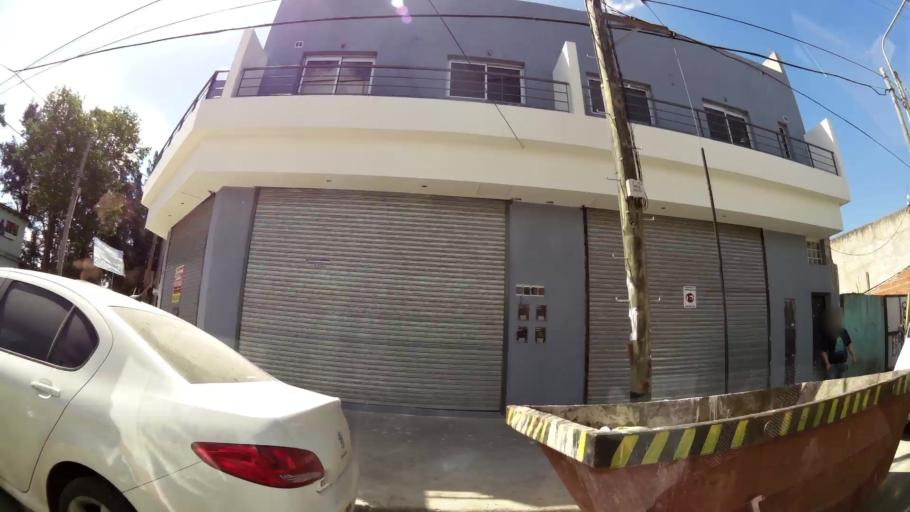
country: AR
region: Buenos Aires
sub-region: Partido de Quilmes
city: Quilmes
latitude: -34.8116
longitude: -58.2696
